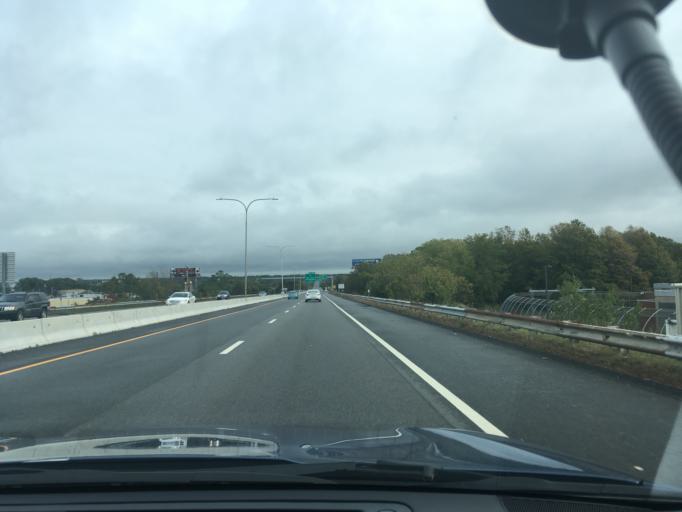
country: US
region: Rhode Island
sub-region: Providence County
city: Cranston
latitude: 41.7514
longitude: -71.4589
